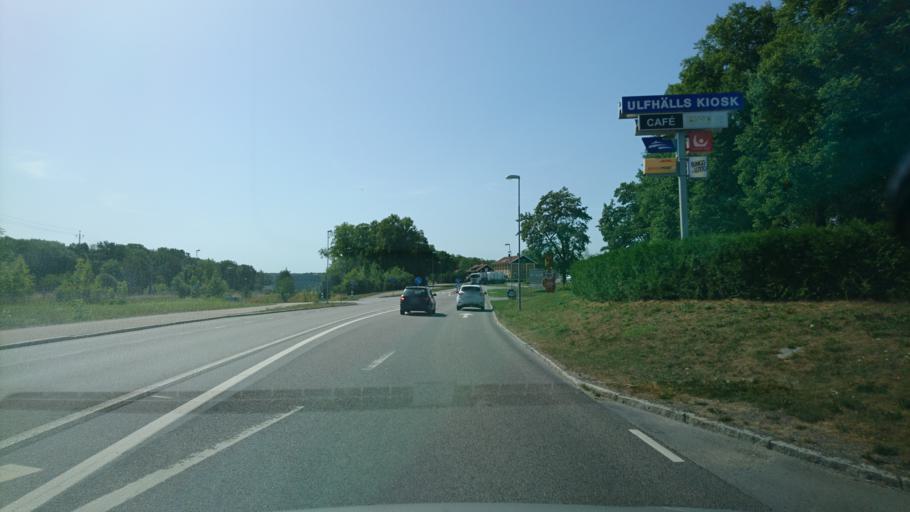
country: SE
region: Soedermanland
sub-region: Strangnas Kommun
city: Strangnas
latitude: 59.3631
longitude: 17.0381
